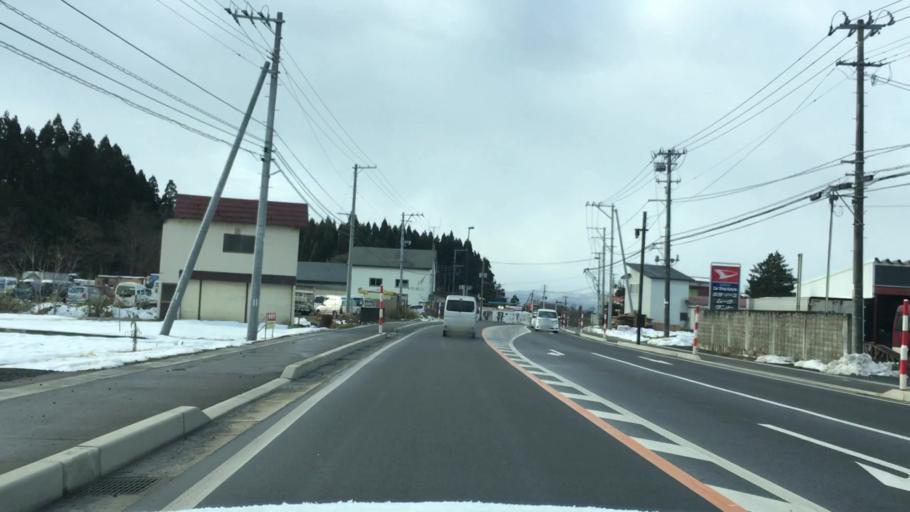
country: JP
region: Akita
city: Odate
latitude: 40.3084
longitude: 140.5689
